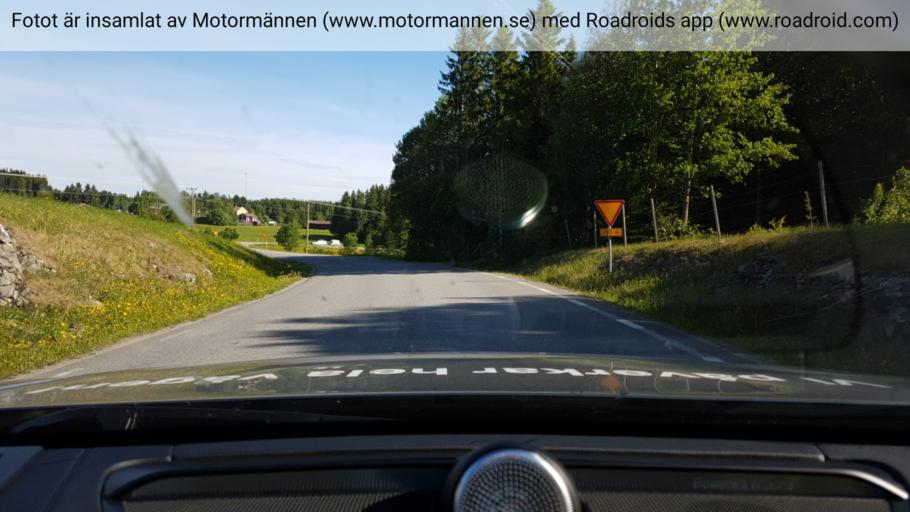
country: SE
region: Jaemtland
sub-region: OEstersunds Kommun
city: Brunflo
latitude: 63.0156
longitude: 14.7344
